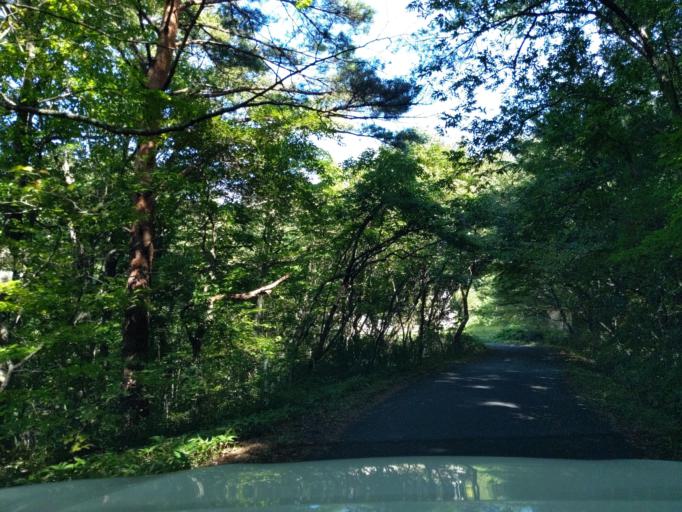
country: JP
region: Fukushima
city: Koriyama
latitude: 37.3974
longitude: 140.2390
